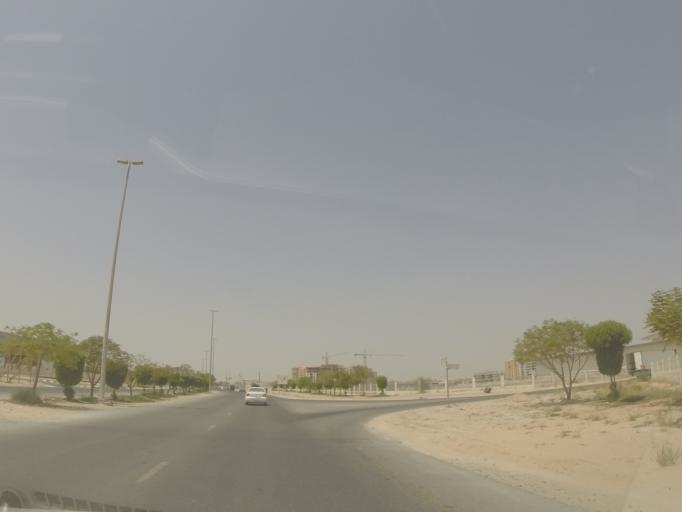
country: AE
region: Dubai
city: Dubai
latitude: 24.9870
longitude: 55.1886
